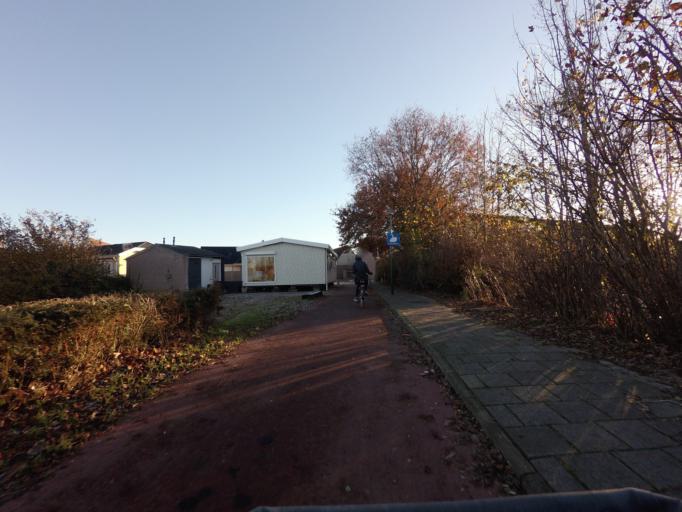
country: NL
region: Utrecht
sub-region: Stichtse Vecht
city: Spechtenkamp
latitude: 52.1459
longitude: 5.0131
